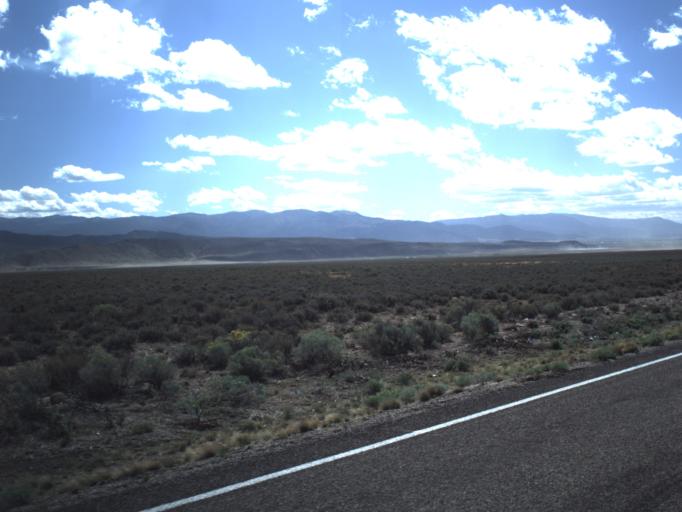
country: US
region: Utah
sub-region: Iron County
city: Enoch
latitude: 37.9402
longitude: -113.0224
